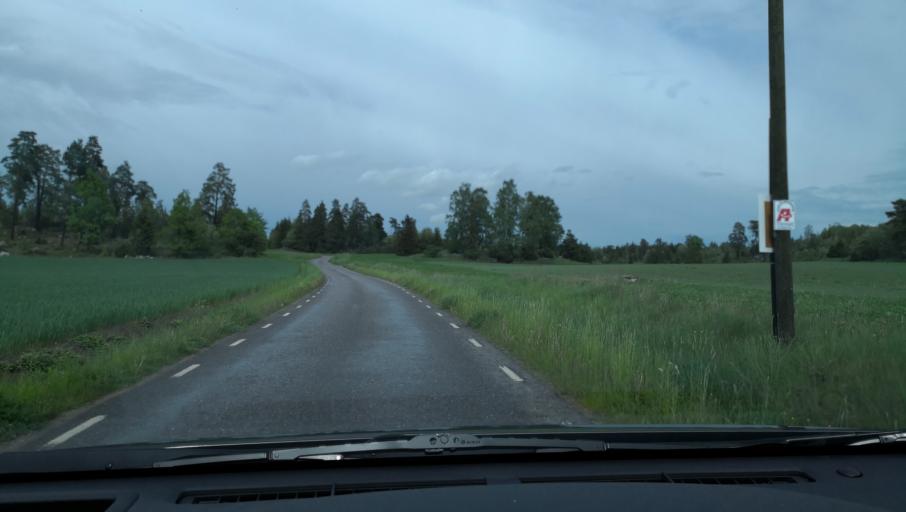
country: SE
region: Uppsala
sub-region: Enkopings Kommun
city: Orsundsbro
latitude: 59.7047
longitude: 17.4197
